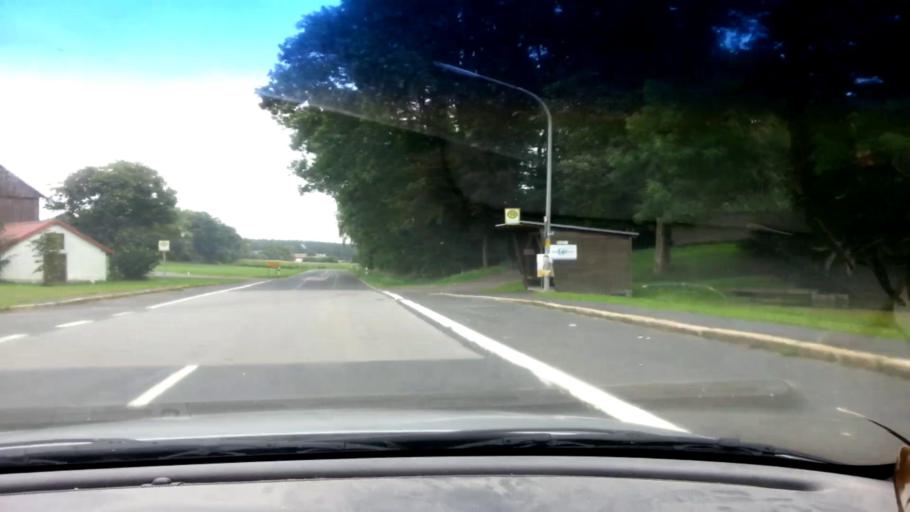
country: DE
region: Bavaria
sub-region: Upper Palatinate
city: Waldsassen
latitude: 50.0357
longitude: 12.2921
